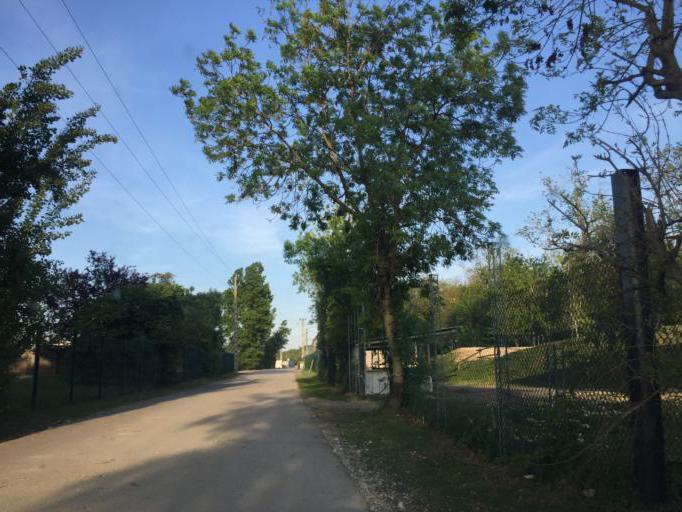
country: FR
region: Rhone-Alpes
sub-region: Departement de l'Ain
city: Saint-Maurice-de-Beynost
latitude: 45.8196
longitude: 4.9936
